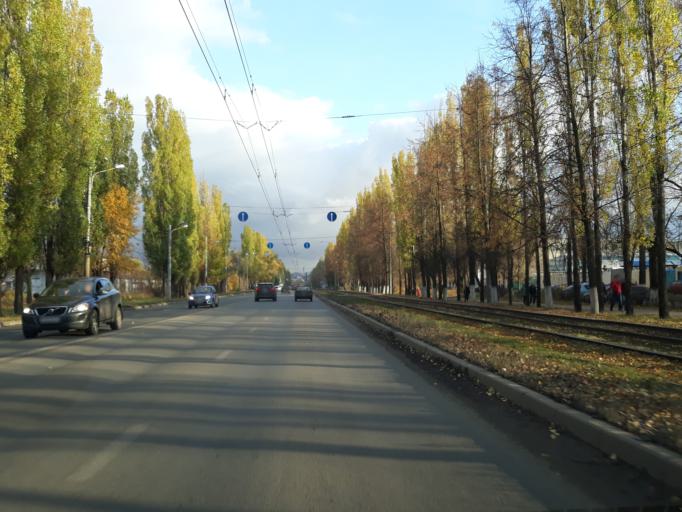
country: RU
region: Nizjnij Novgorod
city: Nizhniy Novgorod
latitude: 56.3357
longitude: 43.8877
